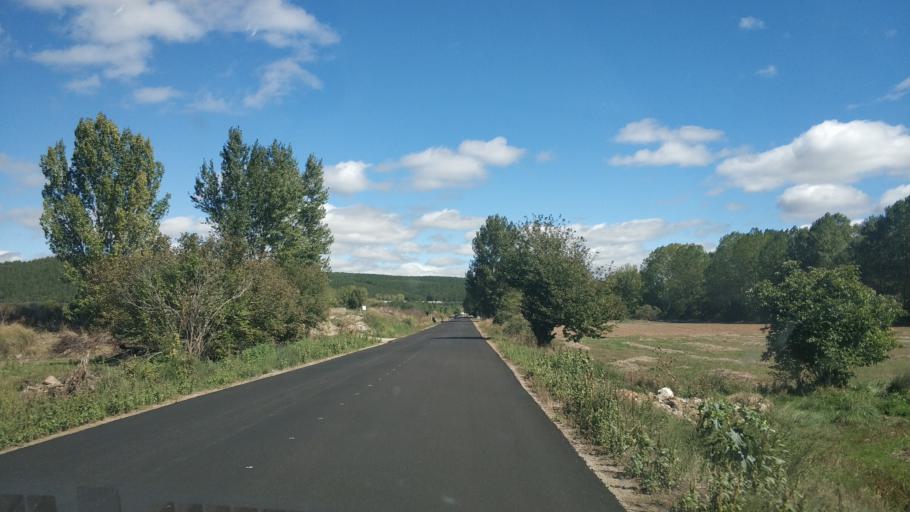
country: ES
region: Castille and Leon
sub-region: Provincia de Burgos
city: Puentedura
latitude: 42.0484
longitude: -3.5712
